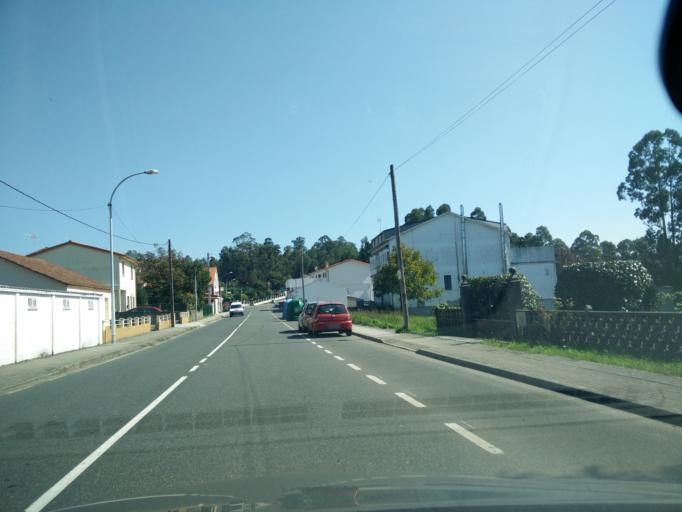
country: ES
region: Galicia
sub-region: Provincia da Coruna
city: Mino
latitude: 43.3402
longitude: -8.1564
